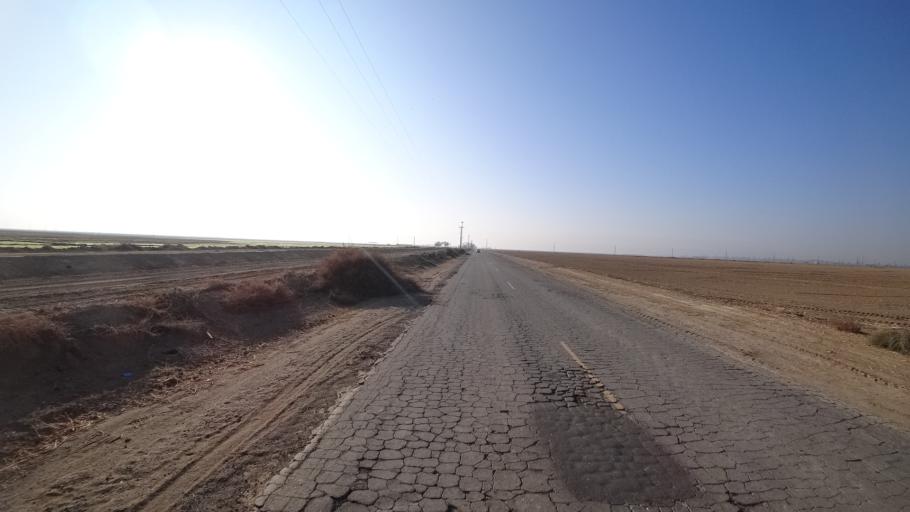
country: US
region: California
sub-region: Kern County
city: Weedpatch
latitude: 35.2284
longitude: -118.9676
